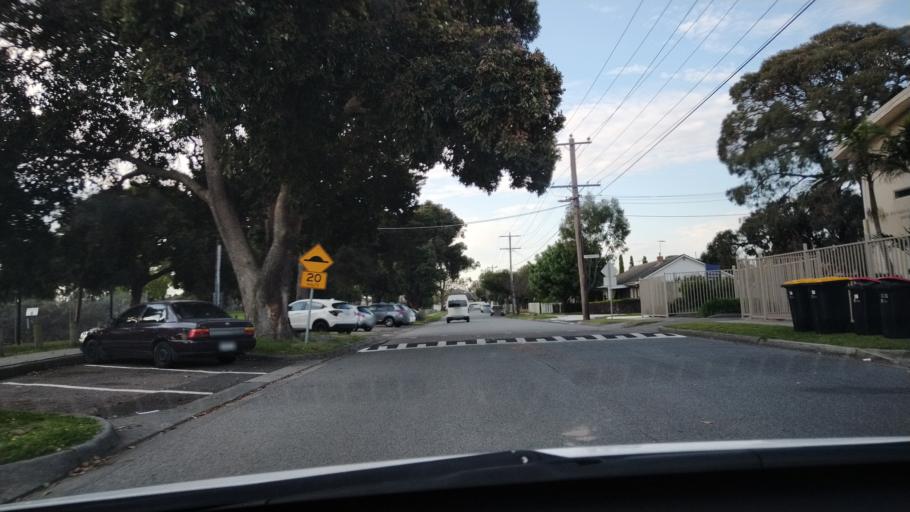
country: AU
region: Victoria
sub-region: Greater Dandenong
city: Springvale South
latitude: -37.9646
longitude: 145.1545
